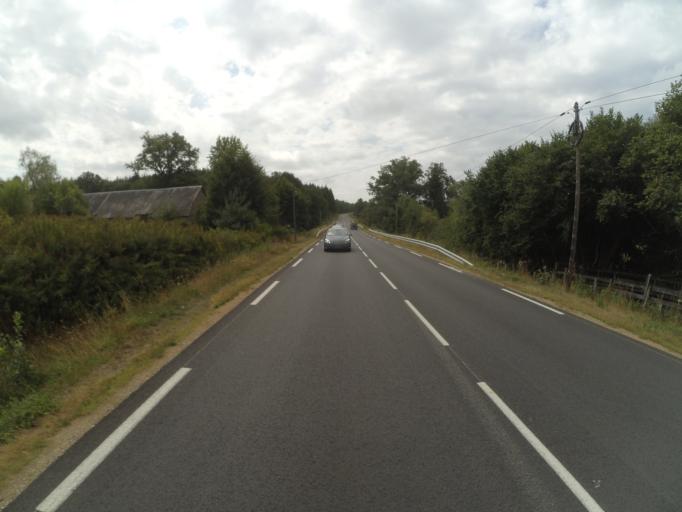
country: FR
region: Limousin
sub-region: Departement de la Creuse
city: La Courtine
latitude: 45.6332
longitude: 2.2772
